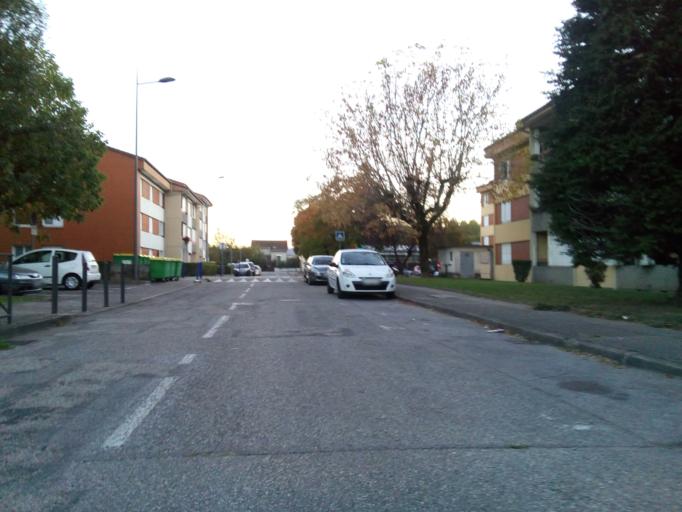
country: FR
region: Rhone-Alpes
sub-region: Departement de l'Isere
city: Saint-Martin-d'Heres
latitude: 45.1806
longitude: 5.7706
